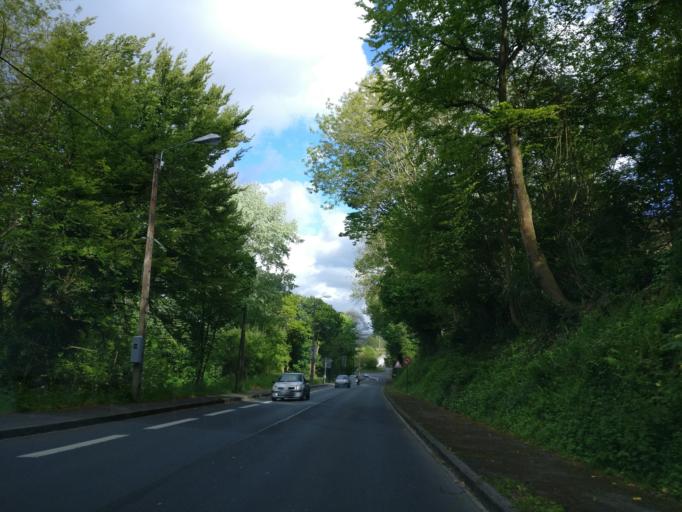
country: FR
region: Brittany
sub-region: Departement du Finistere
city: Brest
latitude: 48.3981
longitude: -4.4391
